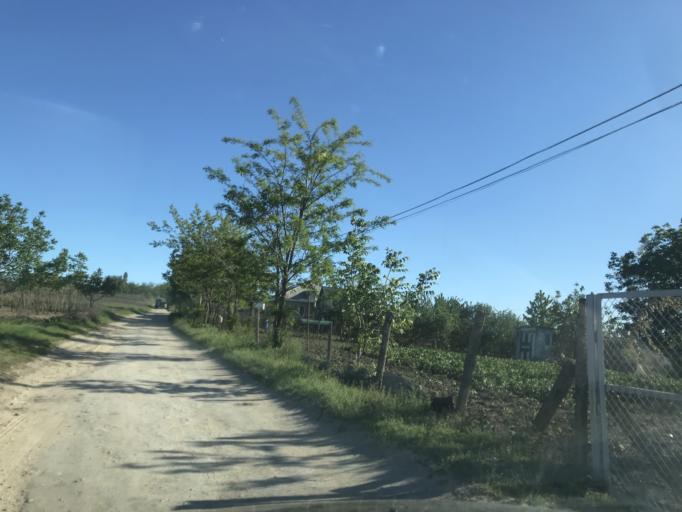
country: MD
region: Chisinau
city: Cricova
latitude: 47.2366
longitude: 28.8154
